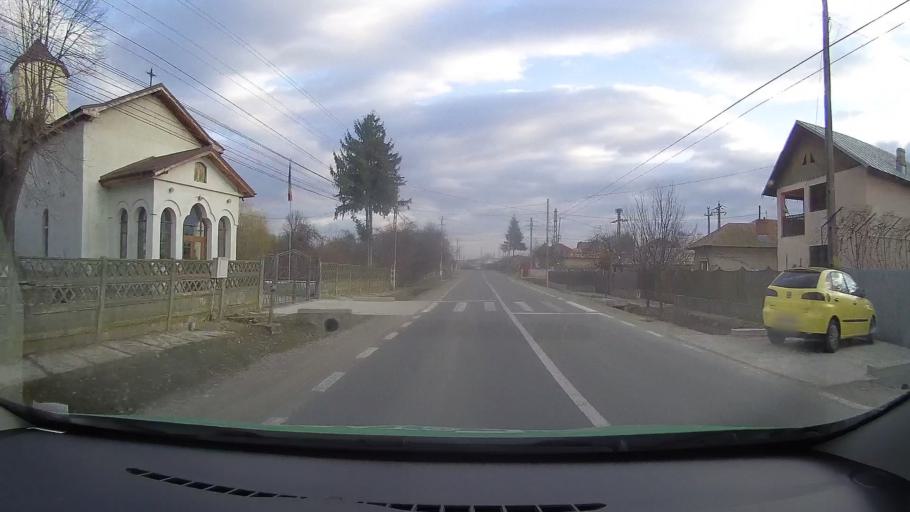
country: RO
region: Dambovita
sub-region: Comuna I. L. Caragiale
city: Ghirdoveni
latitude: 44.9338
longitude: 25.6852
